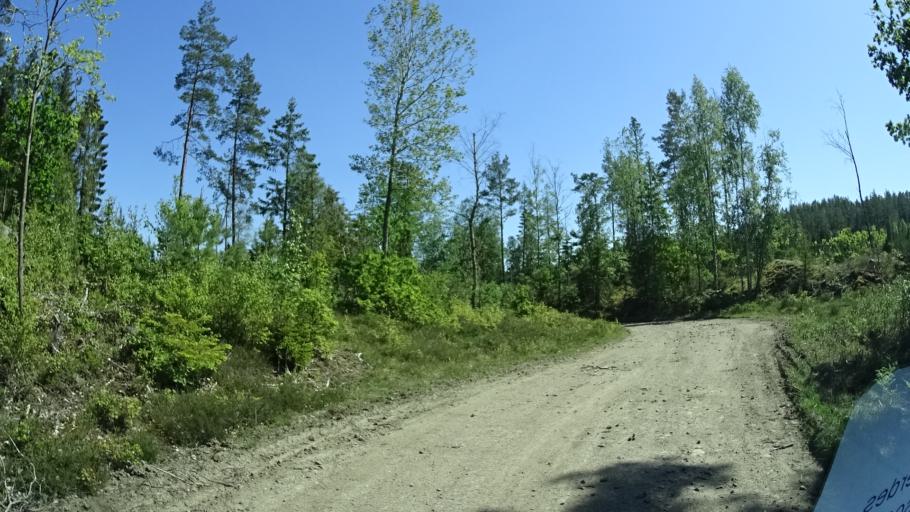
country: SE
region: OEstergoetland
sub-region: Finspangs Kommun
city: Finspang
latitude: 58.6501
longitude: 15.8053
